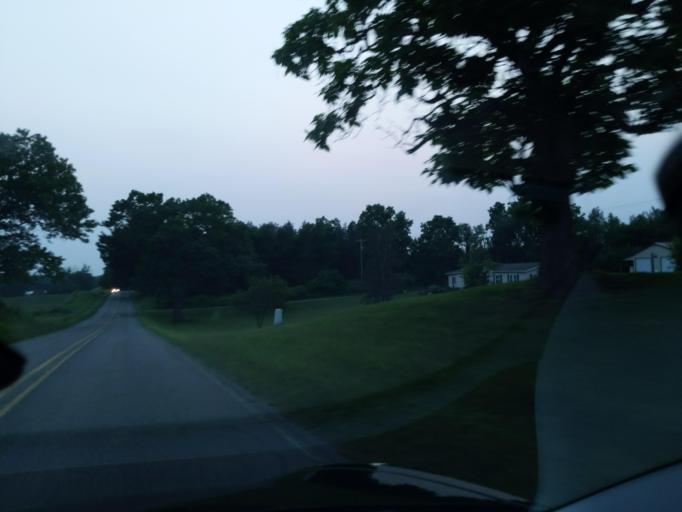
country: US
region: Michigan
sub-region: Ingham County
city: Leslie
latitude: 42.3715
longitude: -84.5305
